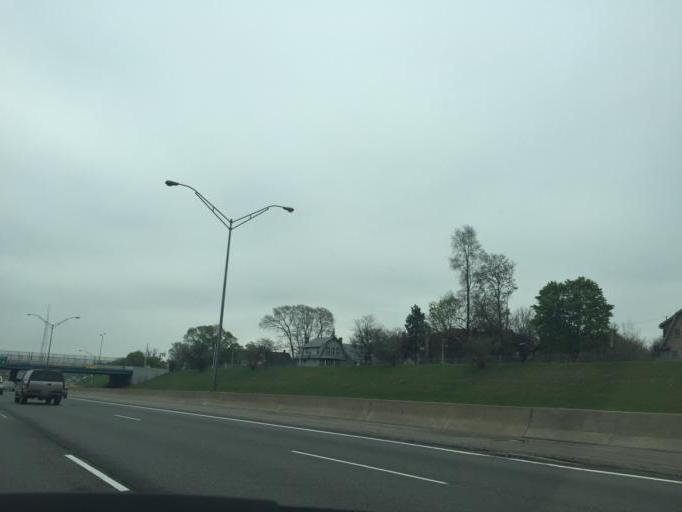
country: US
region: Michigan
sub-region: Wayne County
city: Dearborn
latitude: 42.3853
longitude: -83.1613
